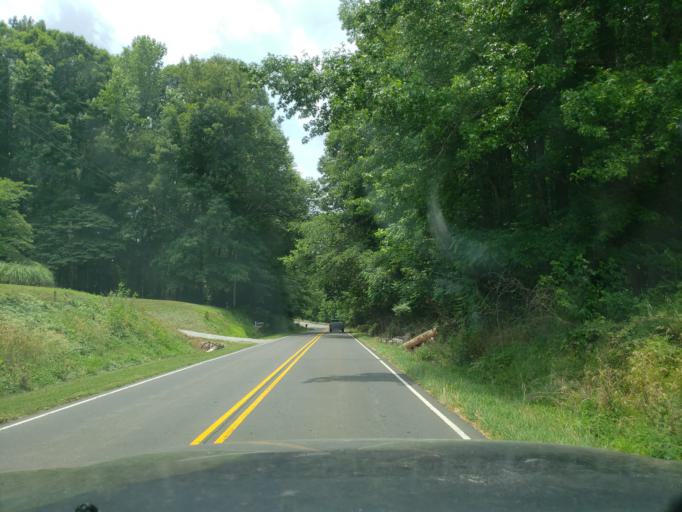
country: US
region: North Carolina
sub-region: Durham County
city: Gorman
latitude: 36.1541
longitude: -78.8997
